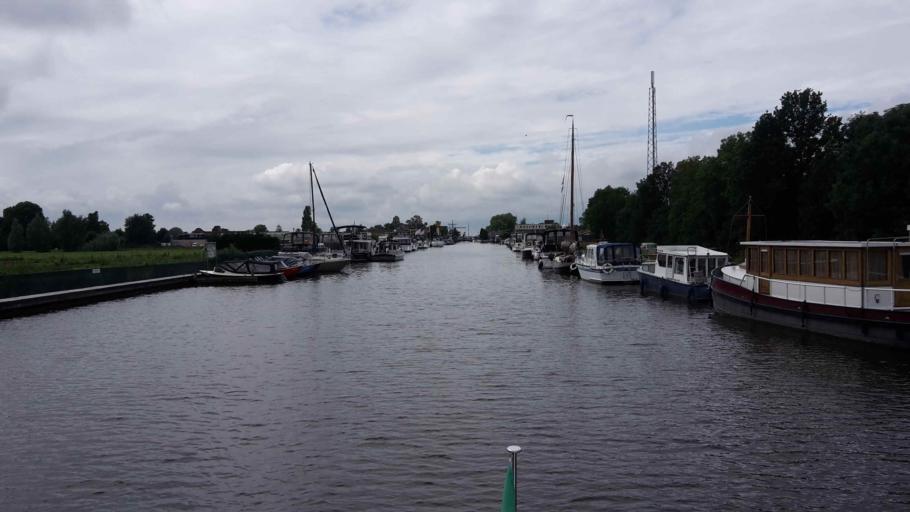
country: NL
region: Friesland
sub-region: Gemeente Lemsterland
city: Echtenerbrug
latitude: 52.8710
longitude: 5.8301
